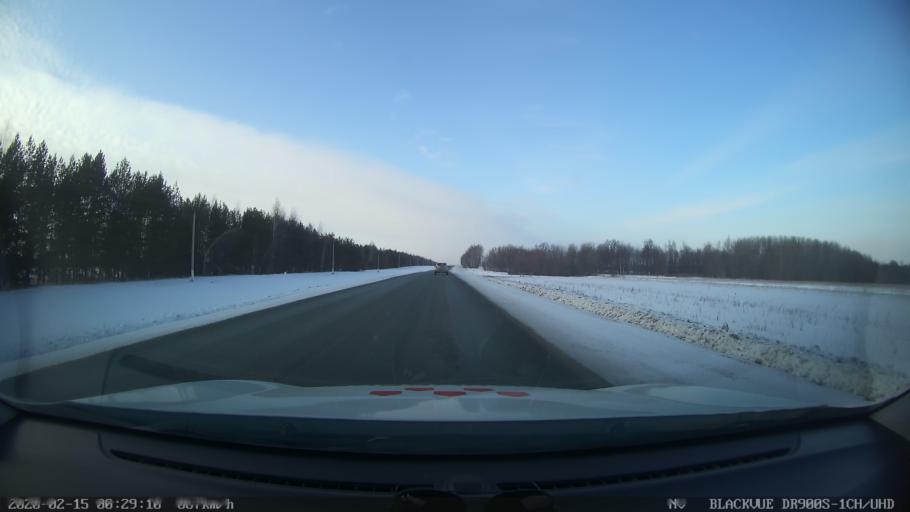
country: RU
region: Tatarstan
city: Verkhniy Uslon
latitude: 55.6484
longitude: 48.8713
